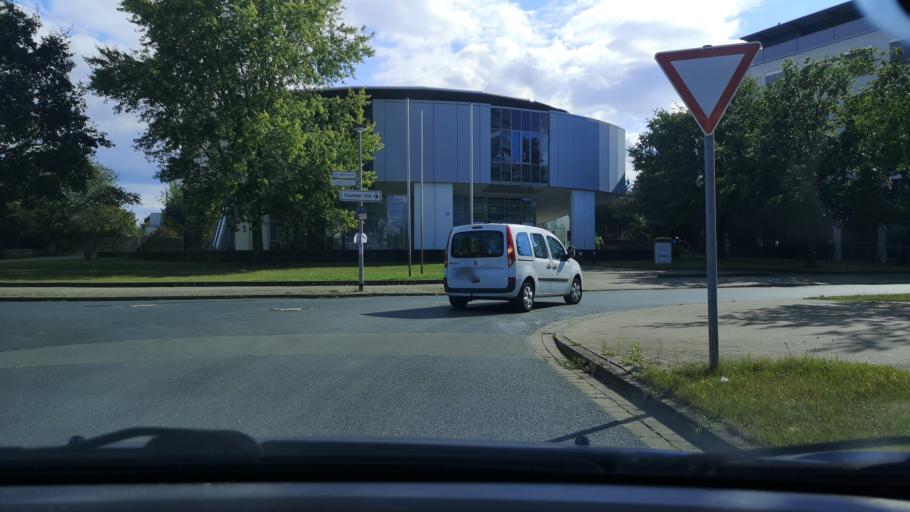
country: DE
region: Lower Saxony
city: Hannover
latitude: 52.3900
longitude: 9.7983
